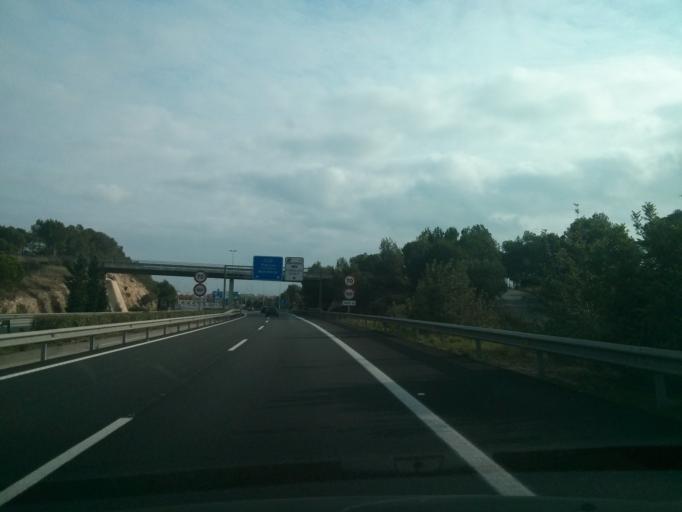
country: ES
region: Catalonia
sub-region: Provincia de Tarragona
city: Cunit
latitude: 41.2091
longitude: 1.6447
